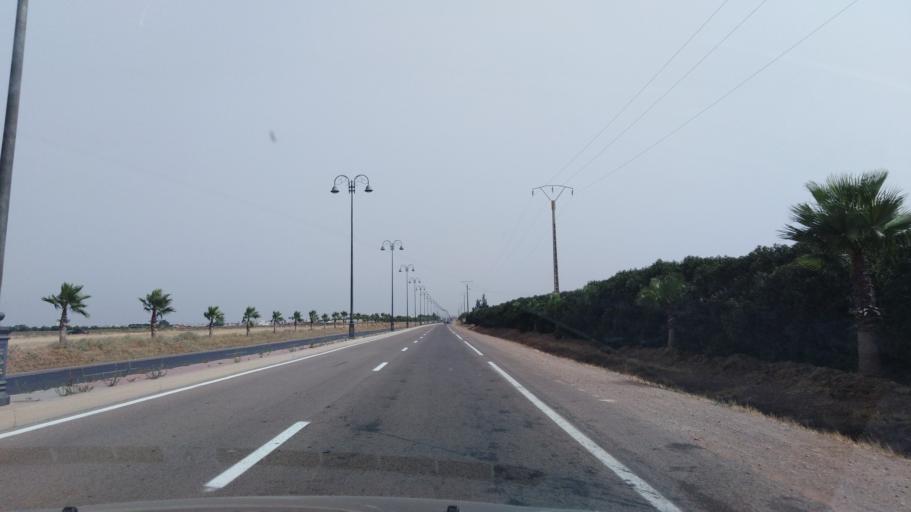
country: MA
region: Chaouia-Ouardigha
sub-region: Settat Province
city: Berrechid
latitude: 33.2984
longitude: -7.5979
